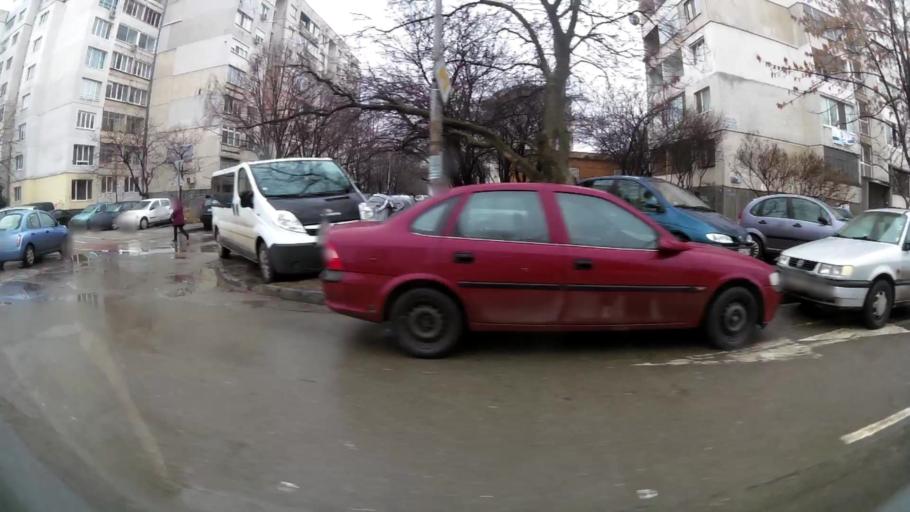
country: BG
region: Sofia-Capital
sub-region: Stolichna Obshtina
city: Sofia
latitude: 42.6402
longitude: 23.3759
